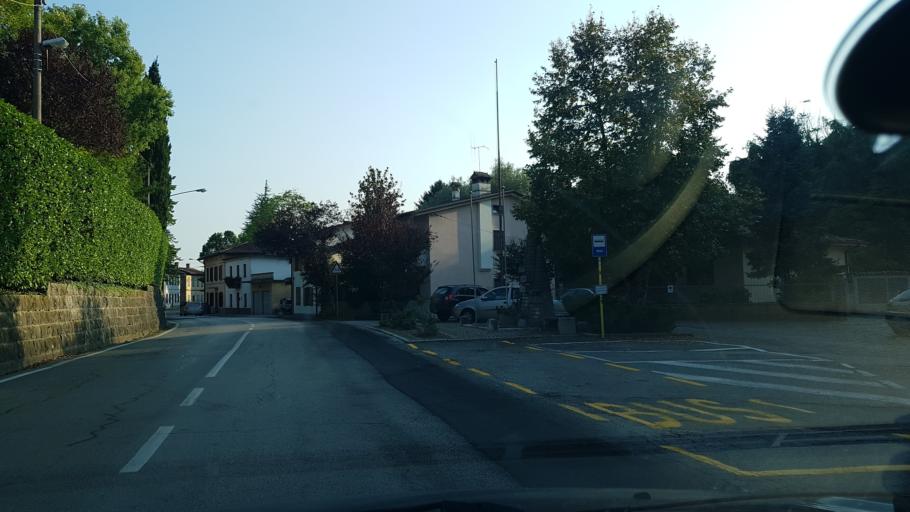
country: IT
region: Friuli Venezia Giulia
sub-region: Provincia di Gorizia
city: Gorizia
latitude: 45.9633
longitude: 13.6150
